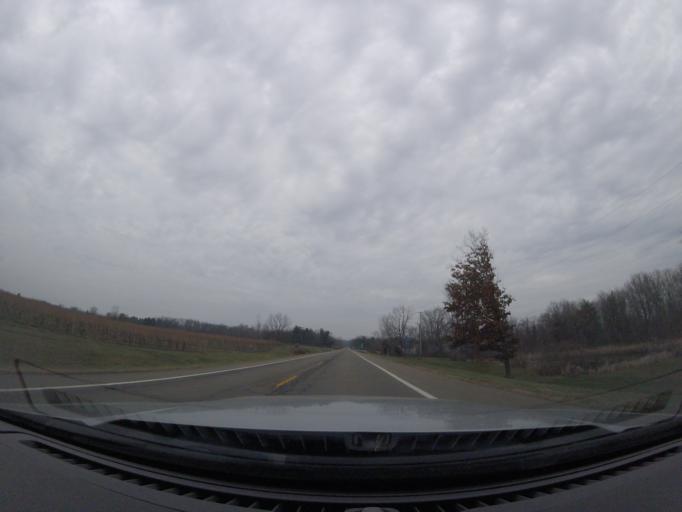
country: US
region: New York
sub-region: Yates County
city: Dundee
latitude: 42.4688
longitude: -76.9186
